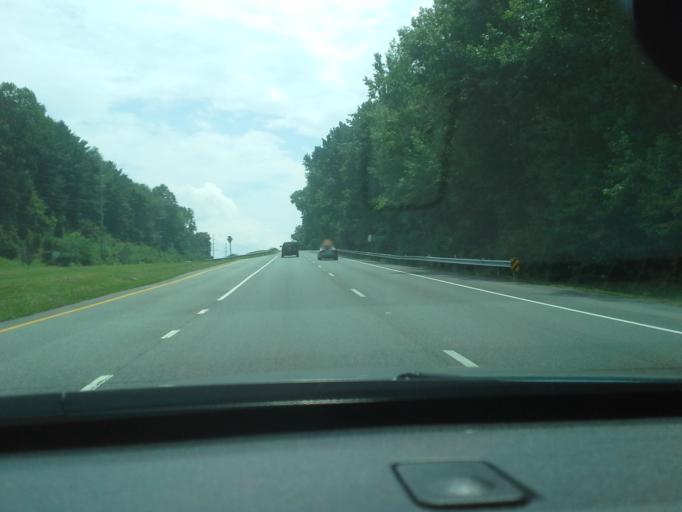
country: US
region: Maryland
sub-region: Calvert County
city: Dunkirk Town Center
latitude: 38.6976
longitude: -76.6438
